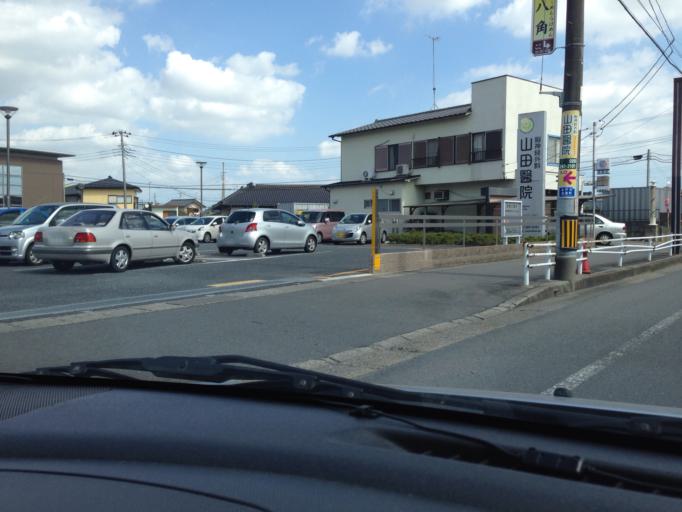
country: JP
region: Ibaraki
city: Mito-shi
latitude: 36.4032
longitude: 140.4340
